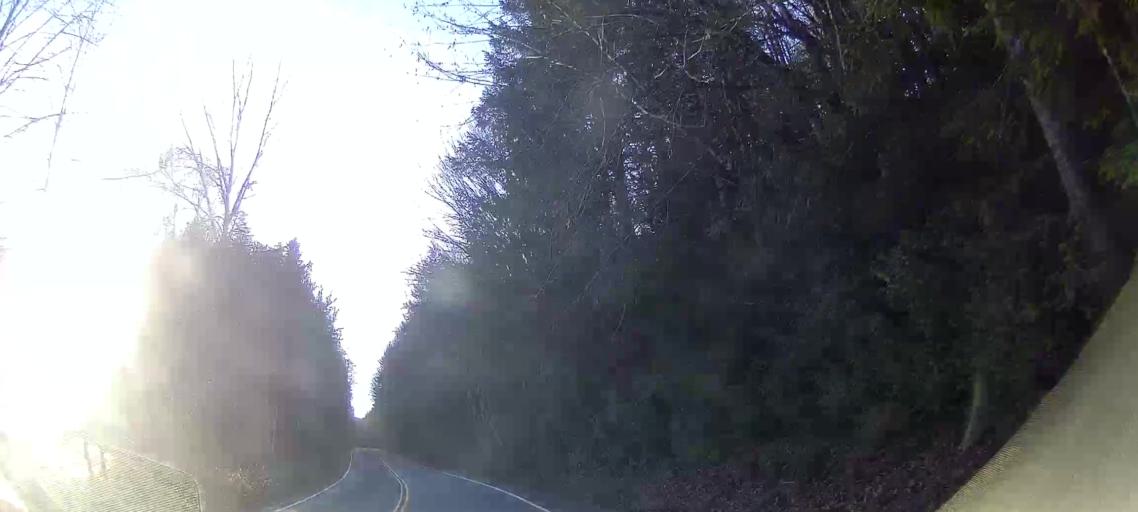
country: US
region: Washington
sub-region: Snohomish County
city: Darrington
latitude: 48.5674
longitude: -121.8032
